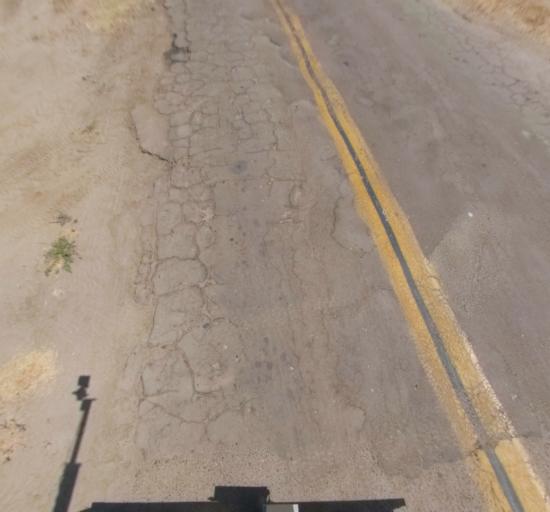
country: US
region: California
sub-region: Madera County
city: Parkwood
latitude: 36.8367
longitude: -120.1827
